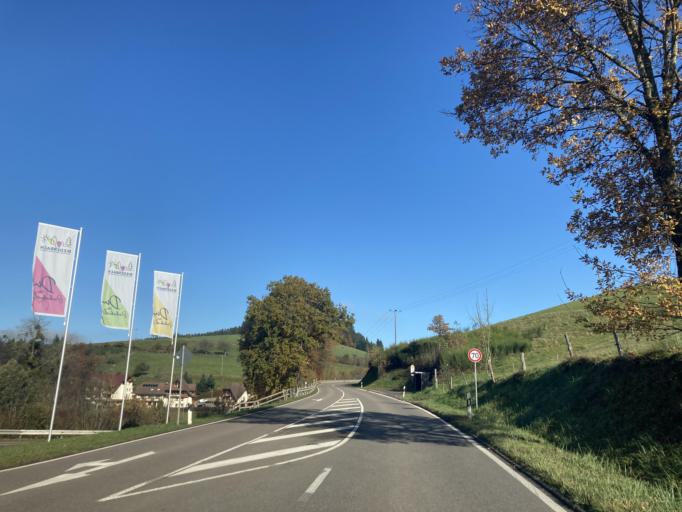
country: DE
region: Baden-Wuerttemberg
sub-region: Freiburg Region
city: Elzach
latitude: 48.1989
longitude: 8.0825
